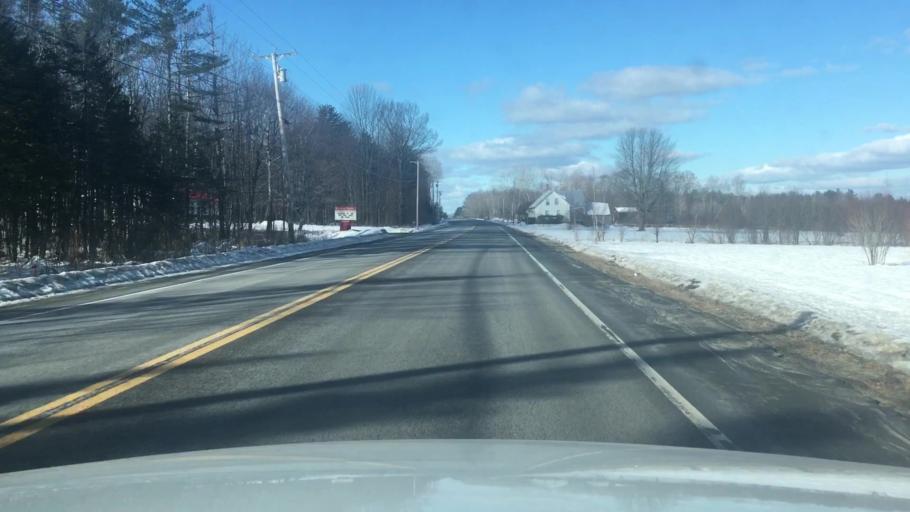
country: US
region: Maine
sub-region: Somerset County
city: Skowhegan
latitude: 44.8173
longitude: -69.7683
